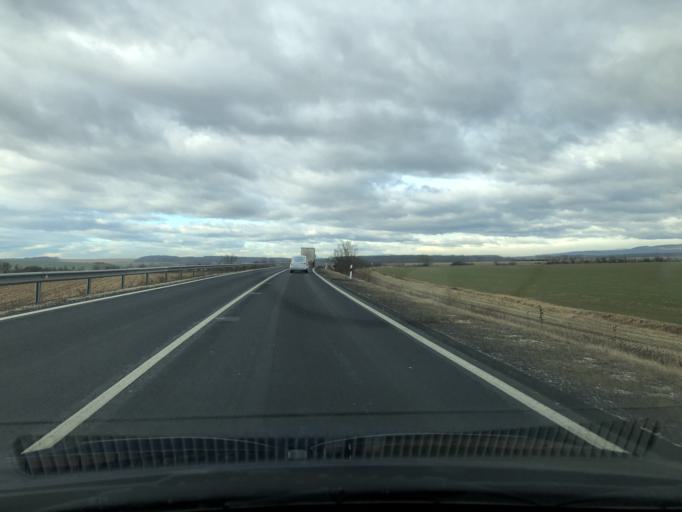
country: HU
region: Vas
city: Gencsapati
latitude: 47.2453
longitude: 16.5203
